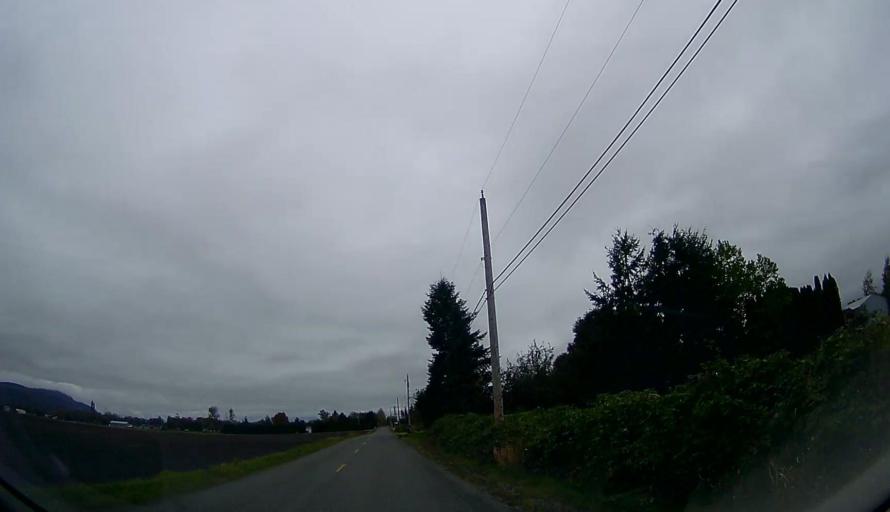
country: US
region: Washington
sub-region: Skagit County
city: Sedro-Woolley
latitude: 48.5146
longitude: -122.1549
